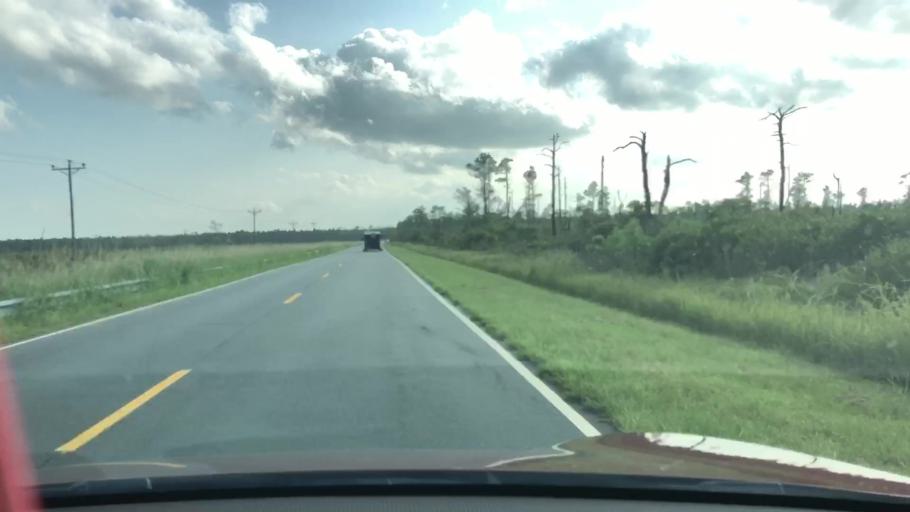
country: US
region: North Carolina
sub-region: Dare County
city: Wanchese
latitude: 35.6137
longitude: -75.7950
